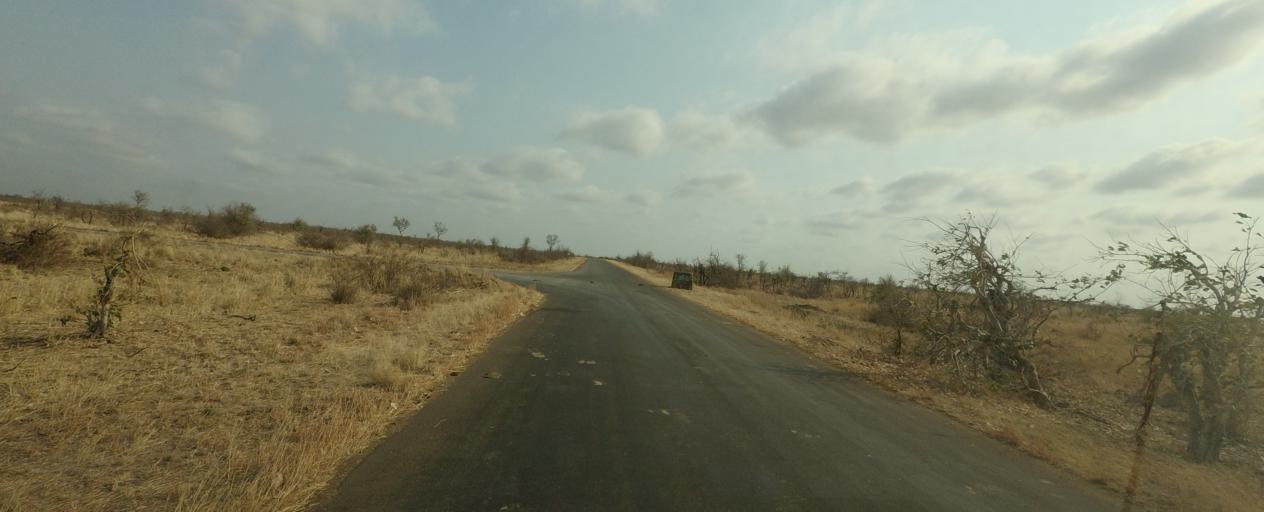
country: ZA
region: Limpopo
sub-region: Vhembe District Municipality
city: Mutale
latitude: -22.9045
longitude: 31.2530
